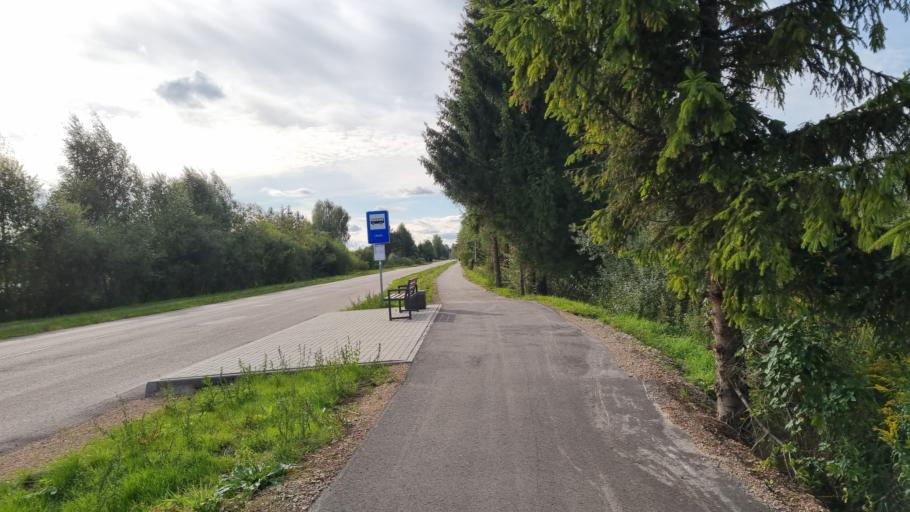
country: LV
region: Olaine
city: Olaine
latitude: 56.6993
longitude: 24.0750
